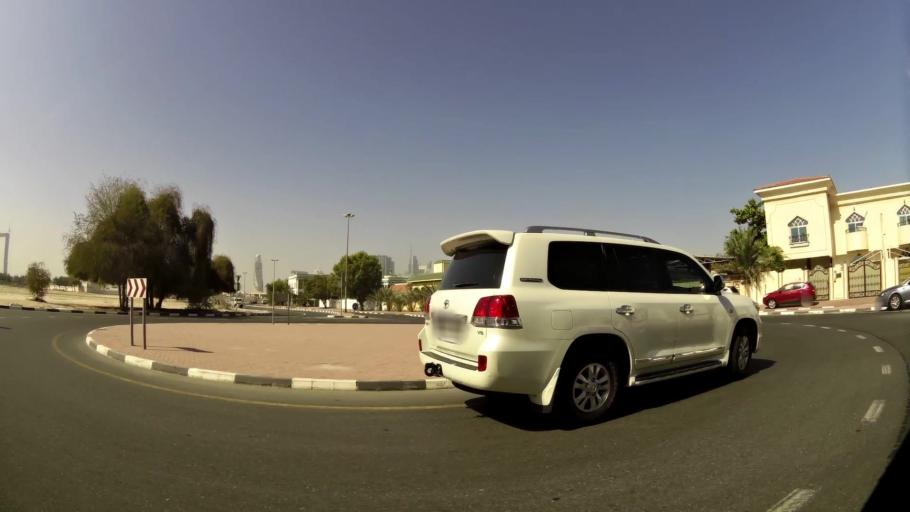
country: AE
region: Ash Shariqah
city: Sharjah
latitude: 25.2467
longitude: 55.2905
